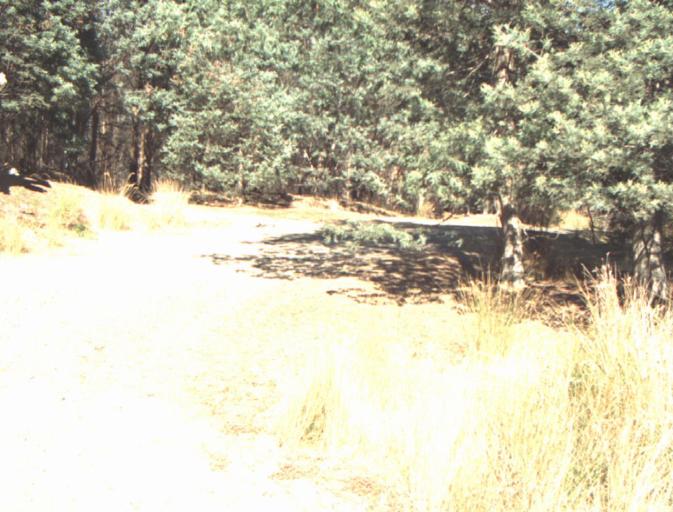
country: AU
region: Tasmania
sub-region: Dorset
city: Scottsdale
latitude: -41.2919
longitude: 147.3538
